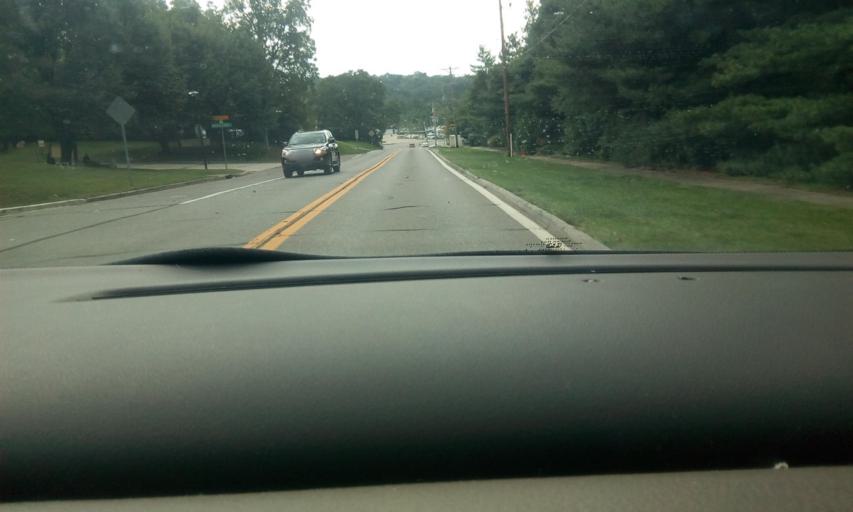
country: US
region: Missouri
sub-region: Saint Louis County
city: Town and Country
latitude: 38.5981
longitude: -90.4795
